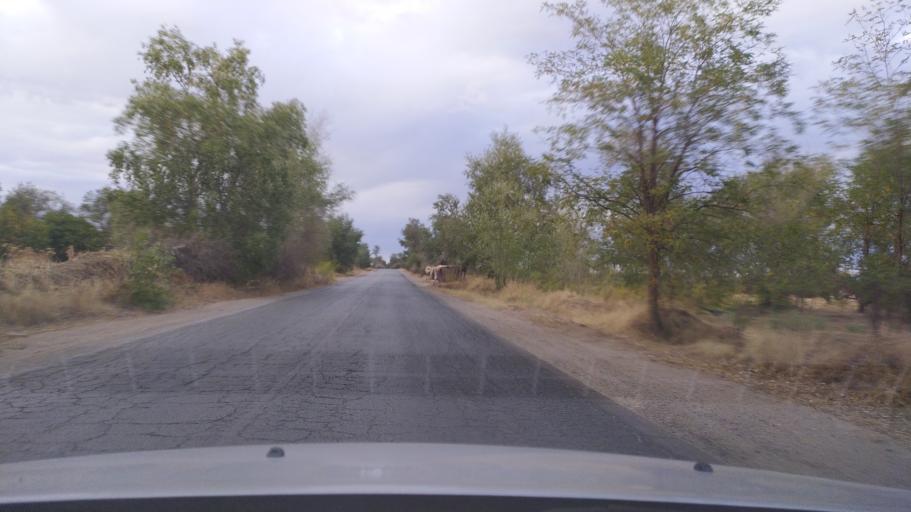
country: DZ
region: Tiaret
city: Frenda
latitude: 35.0358
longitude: 1.0907
